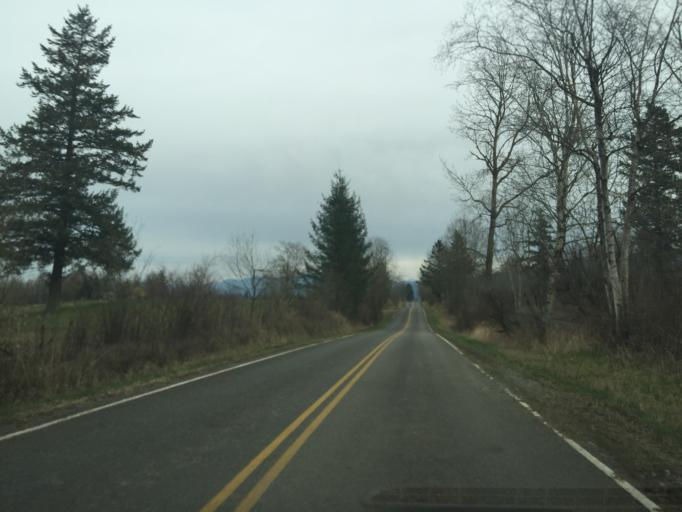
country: US
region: Washington
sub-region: Whatcom County
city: Everson
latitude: 48.9493
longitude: -122.3746
